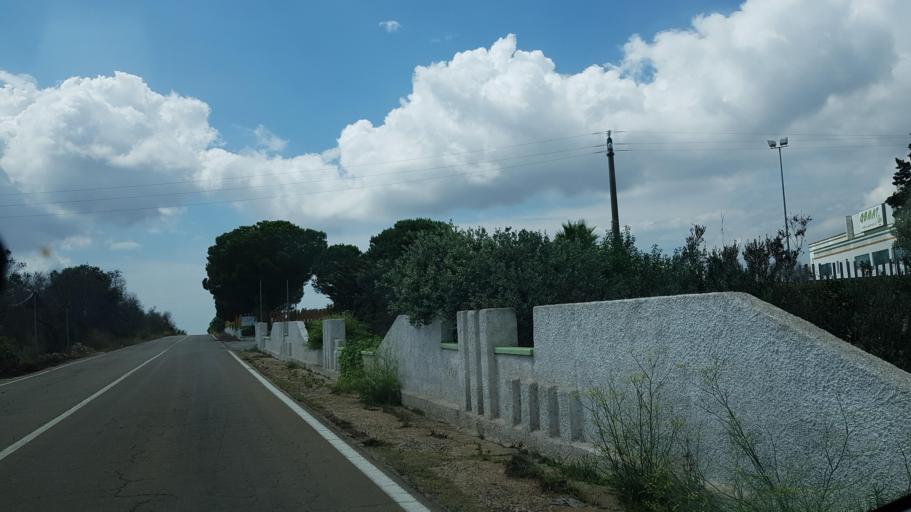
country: IT
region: Apulia
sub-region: Provincia di Lecce
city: Patu
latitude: 39.8452
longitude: 18.3266
